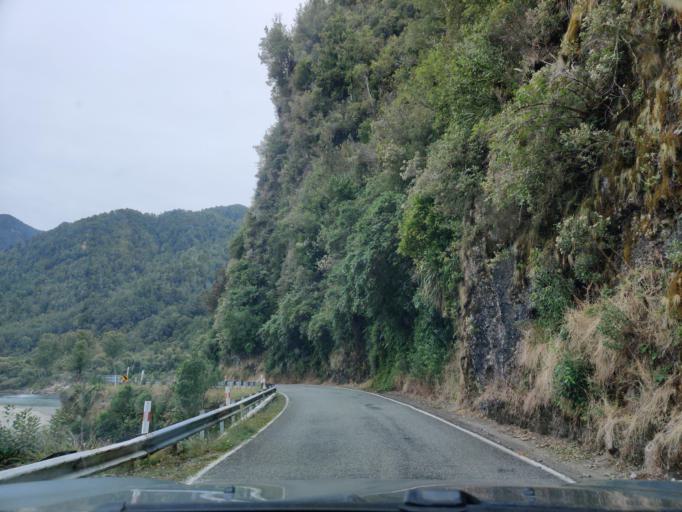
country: NZ
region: West Coast
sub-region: Buller District
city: Westport
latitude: -41.8475
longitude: 171.7425
